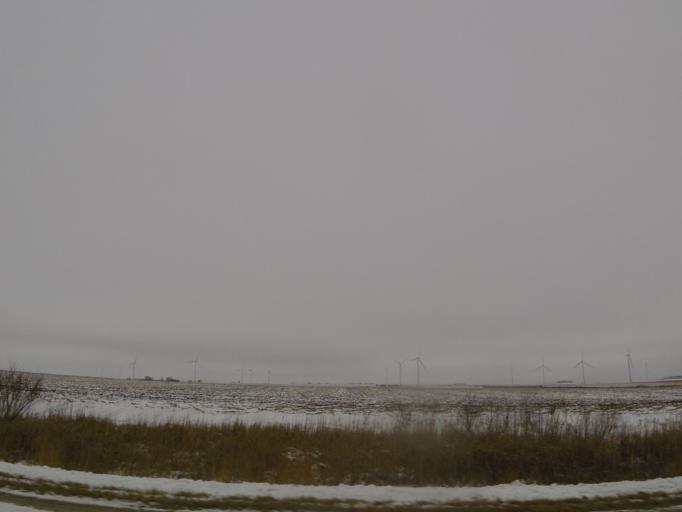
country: US
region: Iowa
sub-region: Howard County
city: Cresco
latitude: 43.3839
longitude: -92.2982
